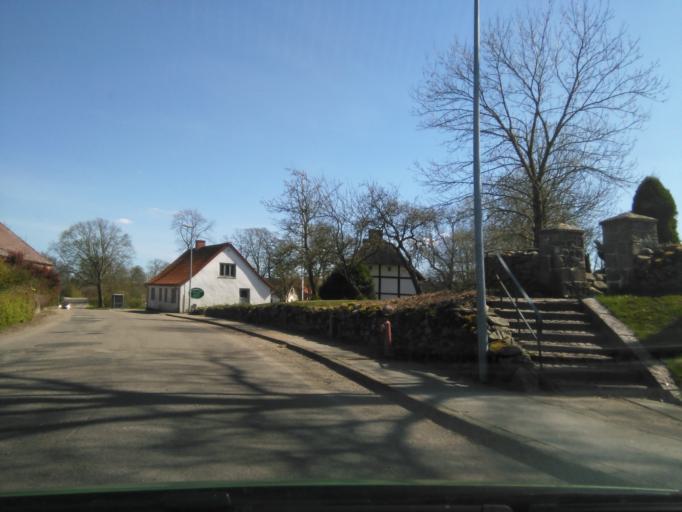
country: DK
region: Central Jutland
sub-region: Silkeborg Kommune
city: Kjellerup
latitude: 56.3506
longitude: 9.3405
